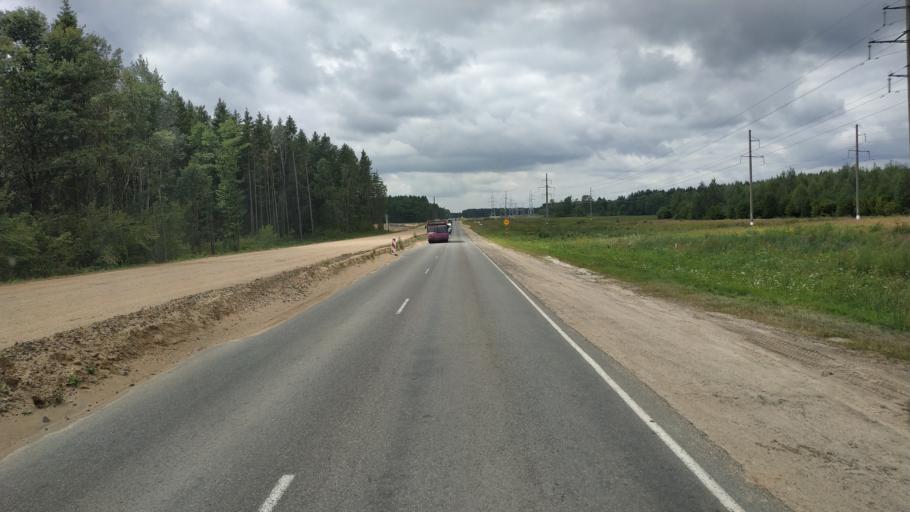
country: BY
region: Mogilev
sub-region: Mahilyowski Rayon
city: Kadino
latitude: 53.8718
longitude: 30.4531
